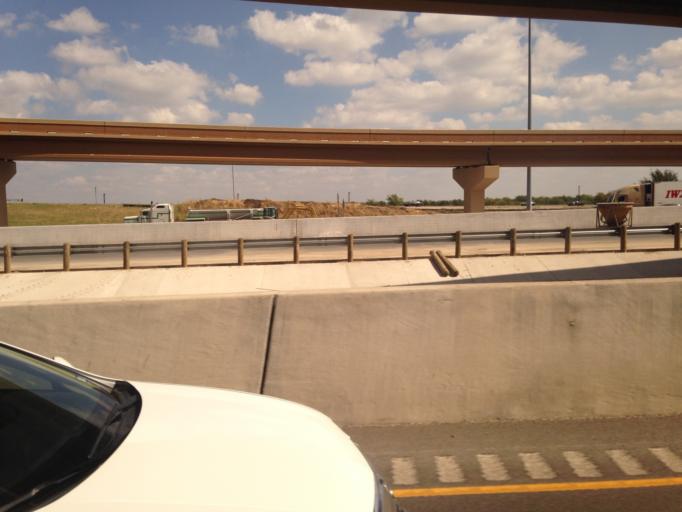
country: US
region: Texas
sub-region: Tarrant County
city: Blue Mound
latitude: 32.8861
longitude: -97.3176
